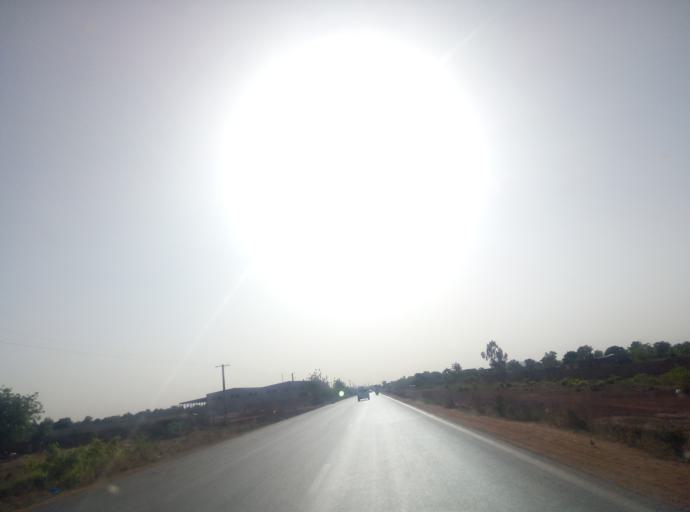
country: ML
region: Bamako
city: Bamako
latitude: 12.5798
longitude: -7.8085
